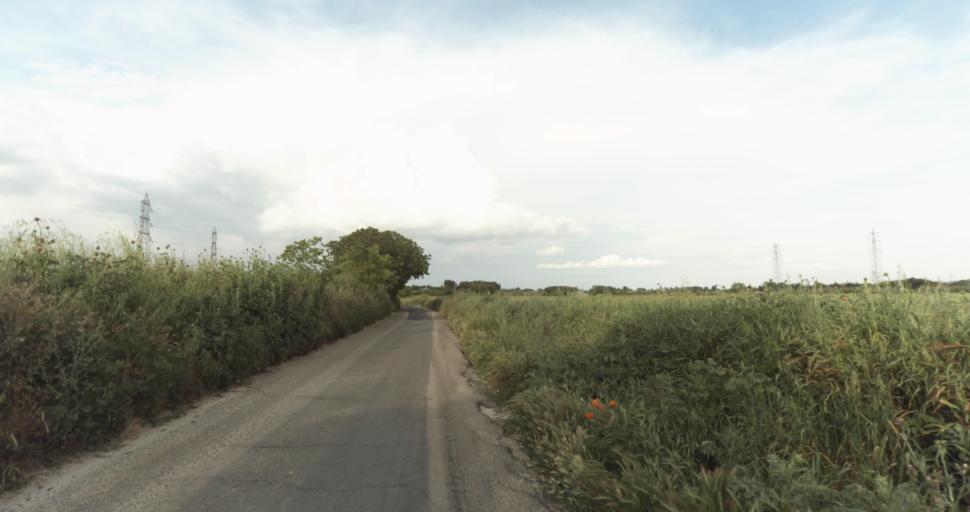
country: FR
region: Languedoc-Roussillon
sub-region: Departement du Gard
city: Nimes
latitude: 43.8072
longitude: 4.3384
